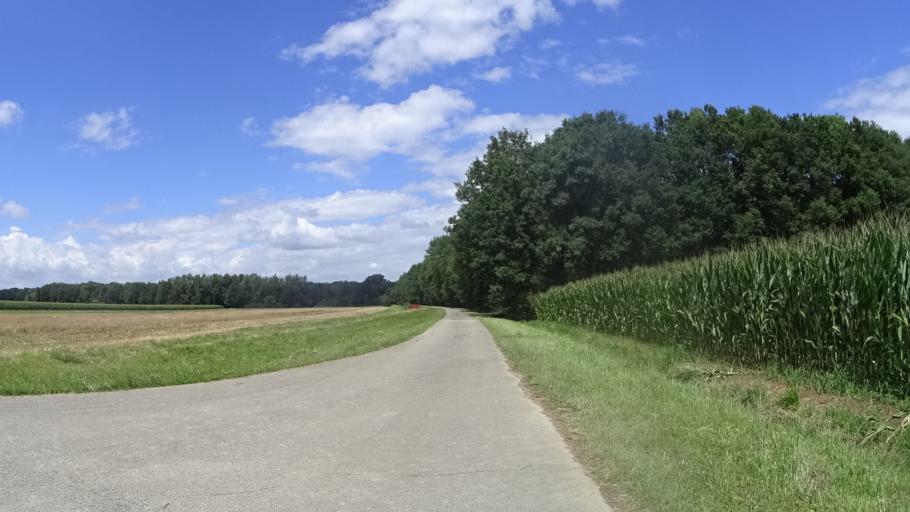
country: FR
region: Champagne-Ardenne
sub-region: Departement de la Haute-Marne
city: Montier-en-Der
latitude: 48.5201
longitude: 4.7726
